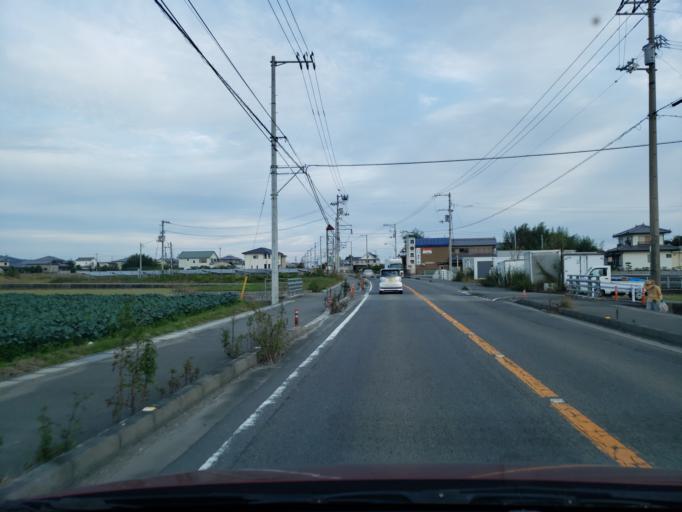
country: JP
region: Tokushima
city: Kamojimacho-jogejima
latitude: 34.0999
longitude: 134.3339
